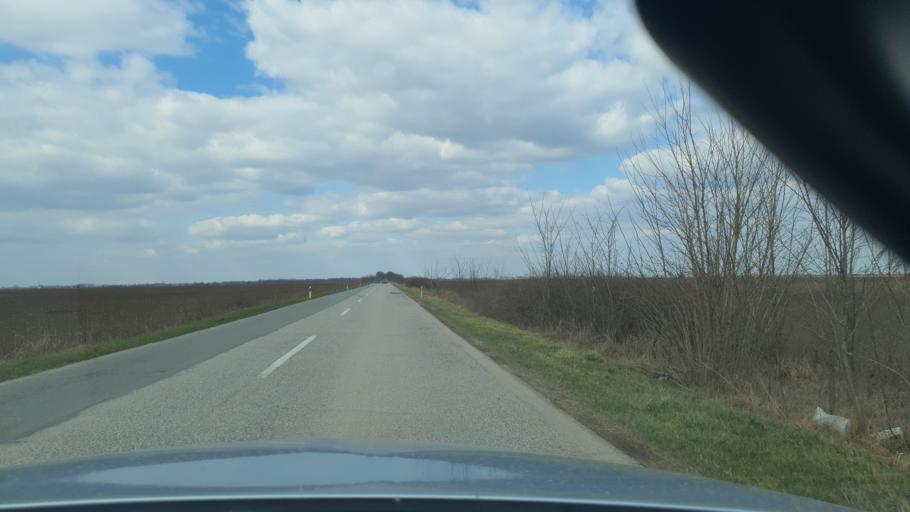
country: RS
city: Obrovac
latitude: 45.4280
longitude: 19.3853
